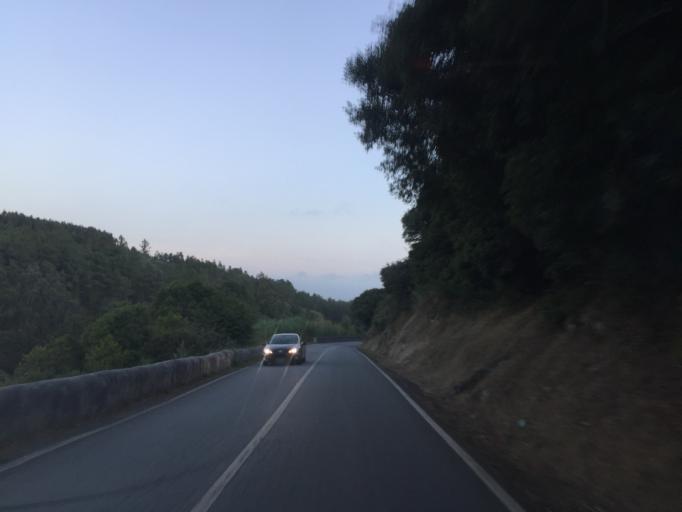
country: PT
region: Leiria
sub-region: Bombarral
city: Bombarral
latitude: 39.2970
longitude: -9.2005
